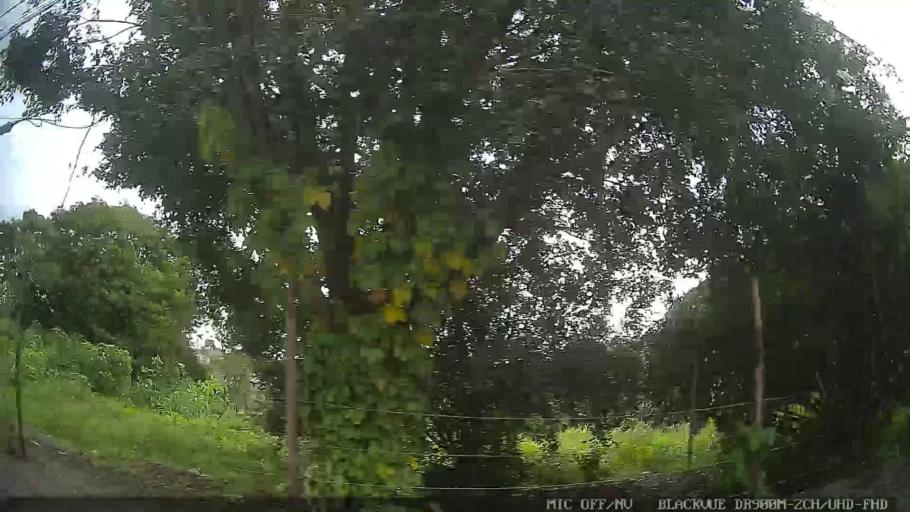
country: BR
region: Sao Paulo
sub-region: Itaquaquecetuba
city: Itaquaquecetuba
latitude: -23.4810
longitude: -46.3008
